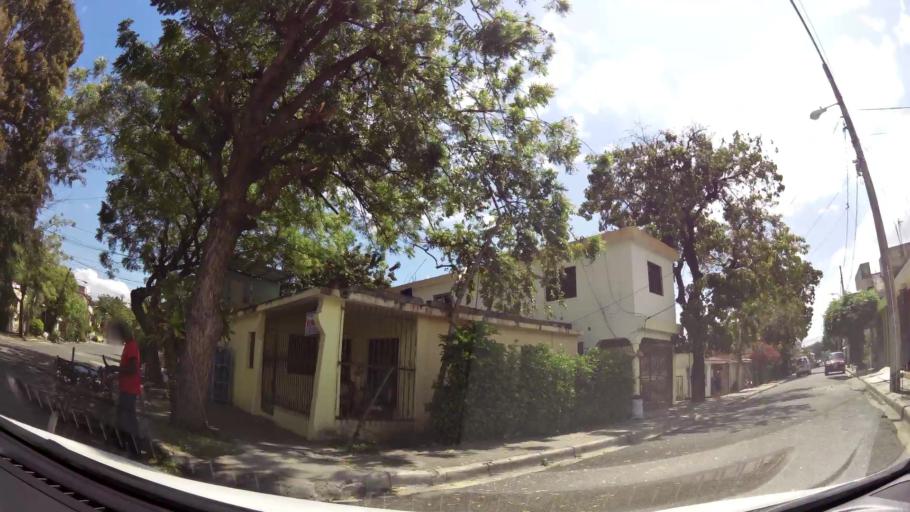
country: DO
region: San Cristobal
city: San Cristobal
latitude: 18.4107
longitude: -70.1104
